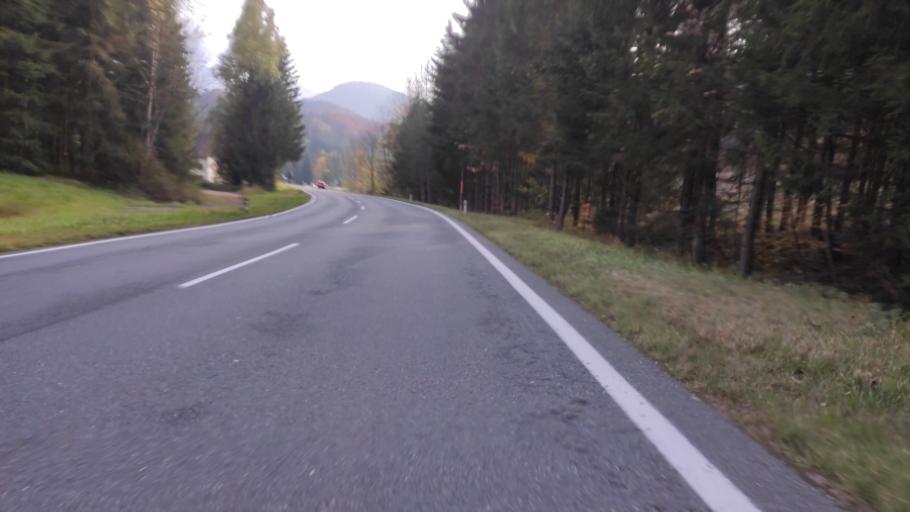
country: AT
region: Salzburg
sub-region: Politischer Bezirk Salzburg-Umgebung
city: Hof bei Salzburg
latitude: 47.8050
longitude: 13.1961
